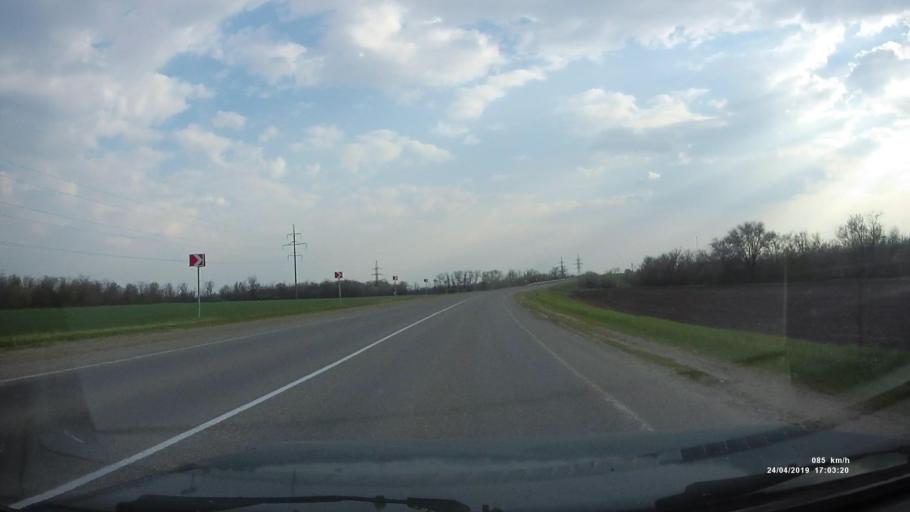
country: RU
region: Rostov
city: Sal'sk
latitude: 46.5669
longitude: 41.6122
